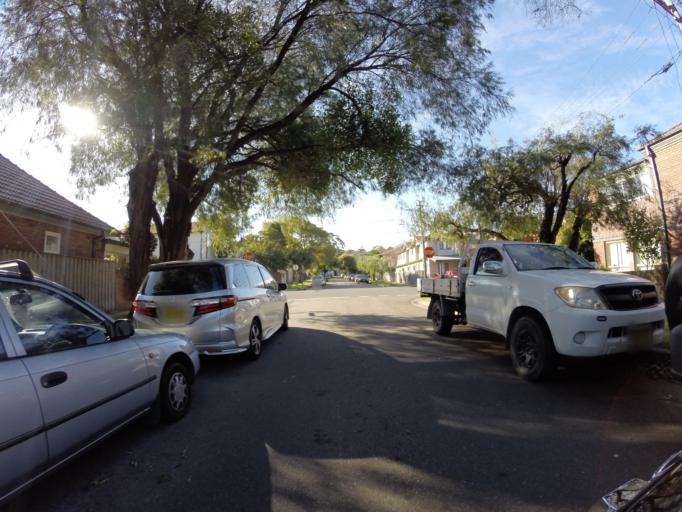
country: AU
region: New South Wales
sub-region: Randwick
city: Randwick
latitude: -33.9166
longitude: 151.2477
